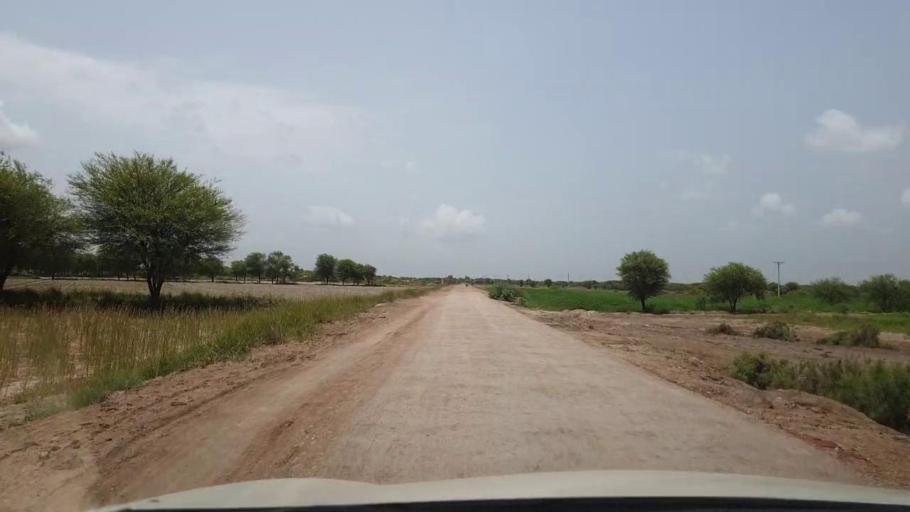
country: PK
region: Sindh
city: Chambar
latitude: 25.2018
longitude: 68.7618
